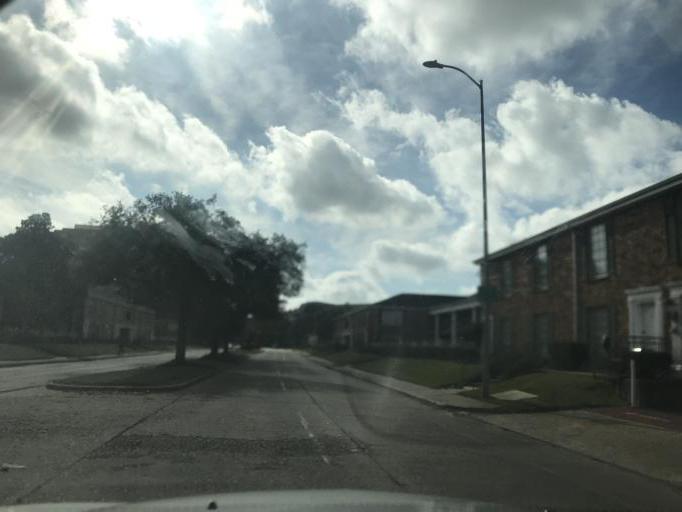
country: US
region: Texas
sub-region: Harris County
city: Hunters Creek Village
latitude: 29.7440
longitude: -95.4854
